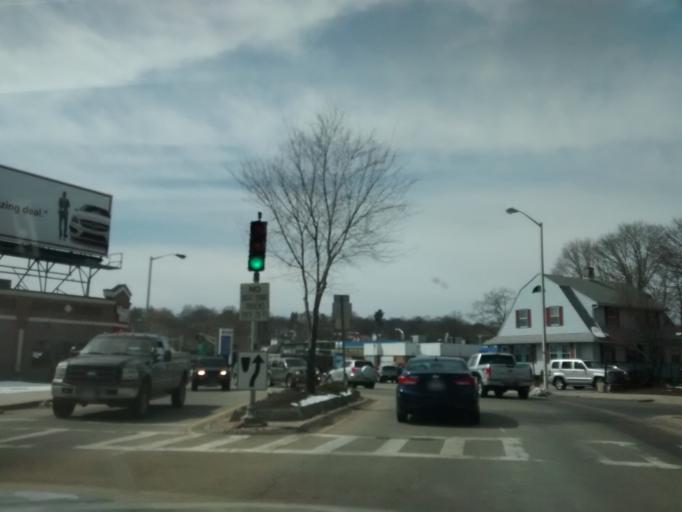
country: US
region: Massachusetts
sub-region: Worcester County
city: Worcester
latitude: 42.2451
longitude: -71.8317
